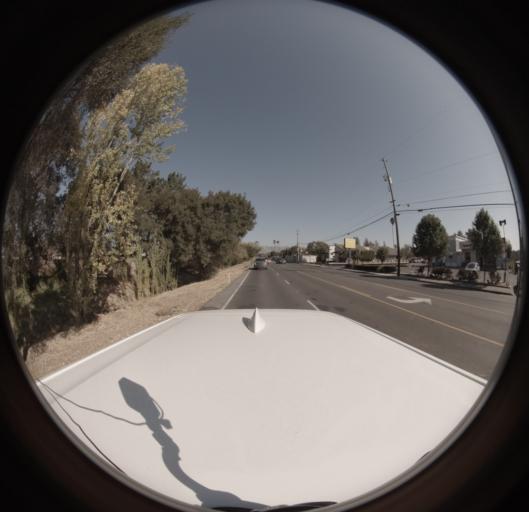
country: US
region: California
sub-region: Sonoma County
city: Petaluma
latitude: 38.2510
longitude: -122.6243
